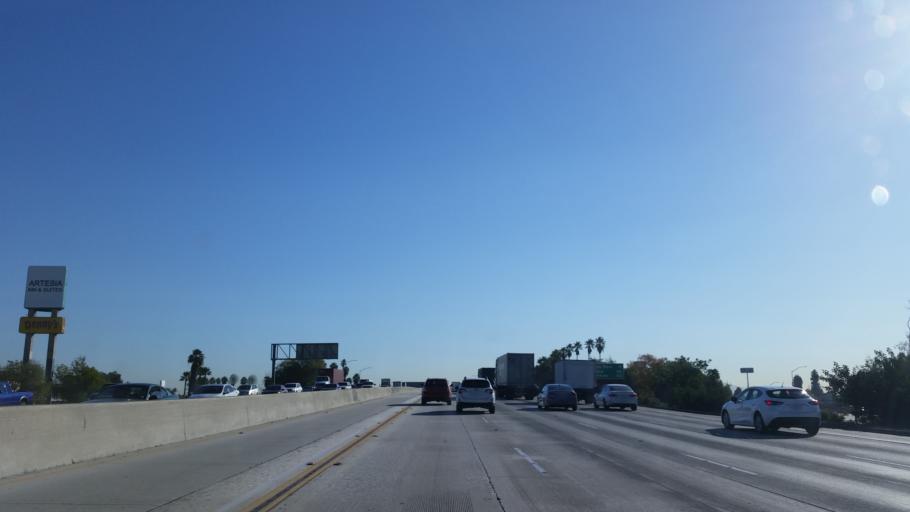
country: US
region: California
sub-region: Los Angeles County
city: Artesia
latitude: 33.8764
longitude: -118.0856
